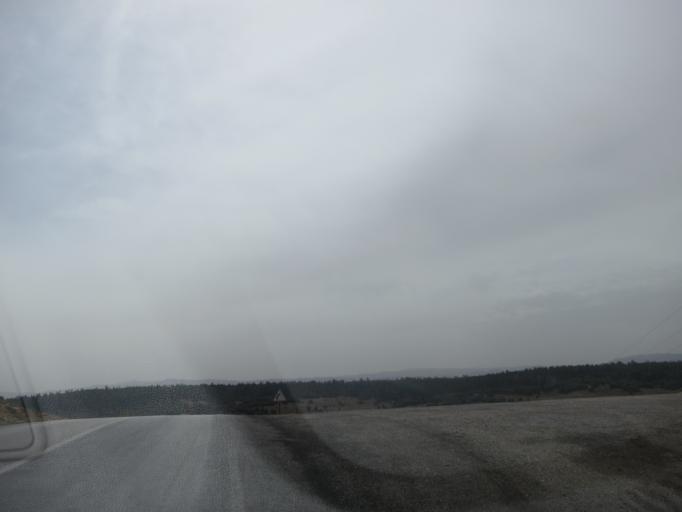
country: MA
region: Meknes-Tafilalet
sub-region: Ifrane
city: Ifrane
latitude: 33.4568
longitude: -5.0375
